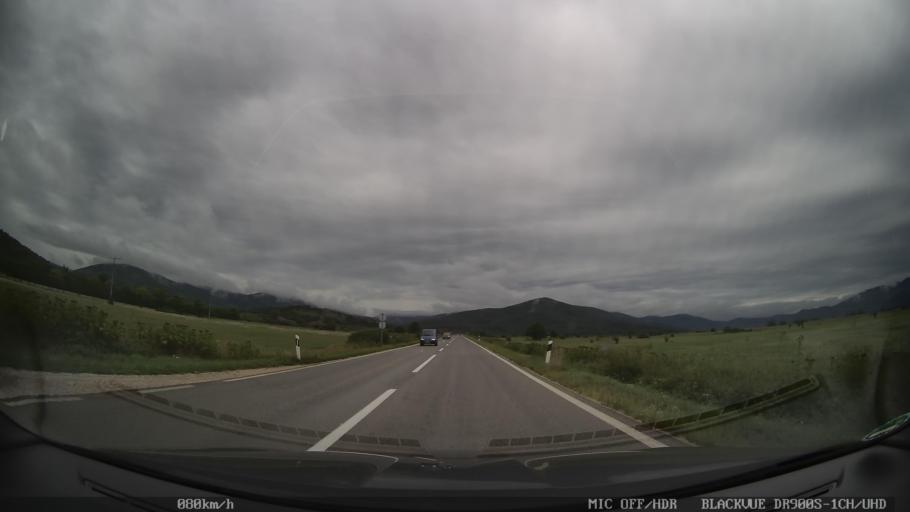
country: HR
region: Licko-Senjska
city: Otocac
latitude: 44.8610
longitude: 15.3082
